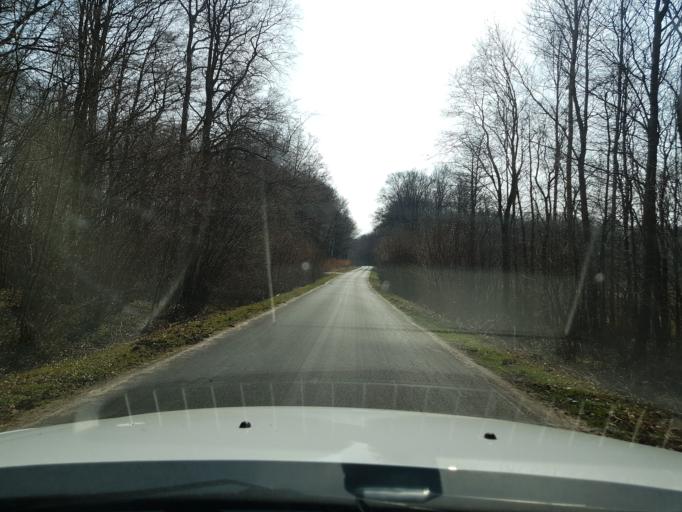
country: PL
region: West Pomeranian Voivodeship
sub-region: Powiat koszalinski
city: Sianow
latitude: 54.2676
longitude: 16.3126
